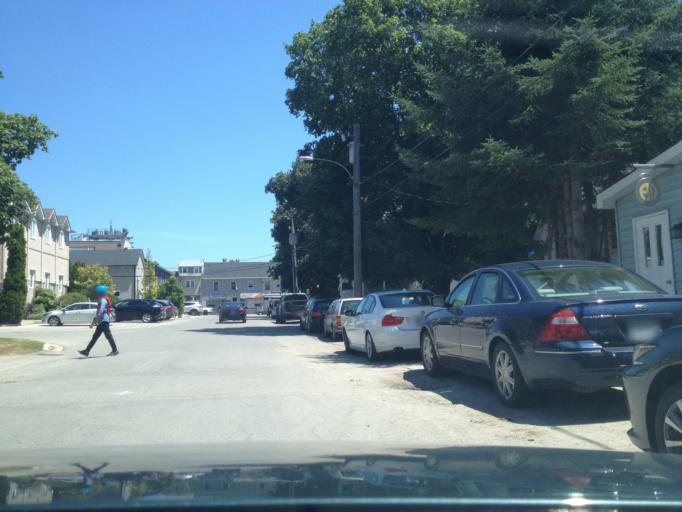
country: CA
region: Ontario
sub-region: Wellington County
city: Guelph
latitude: 43.6824
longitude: -80.4316
